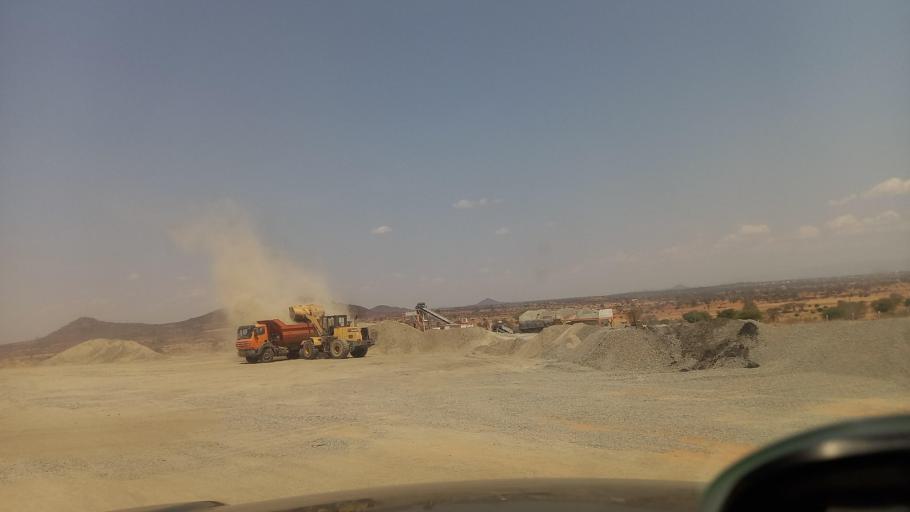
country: TZ
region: Dodoma
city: Msanga
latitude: -6.1799
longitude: 36.0707
